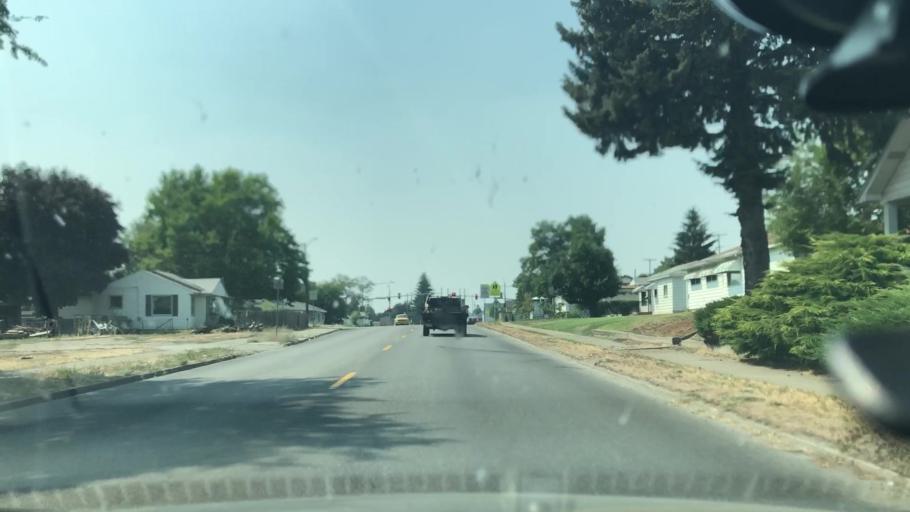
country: US
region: Washington
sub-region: Spokane County
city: Millwood
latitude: 47.6858
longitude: -117.3550
